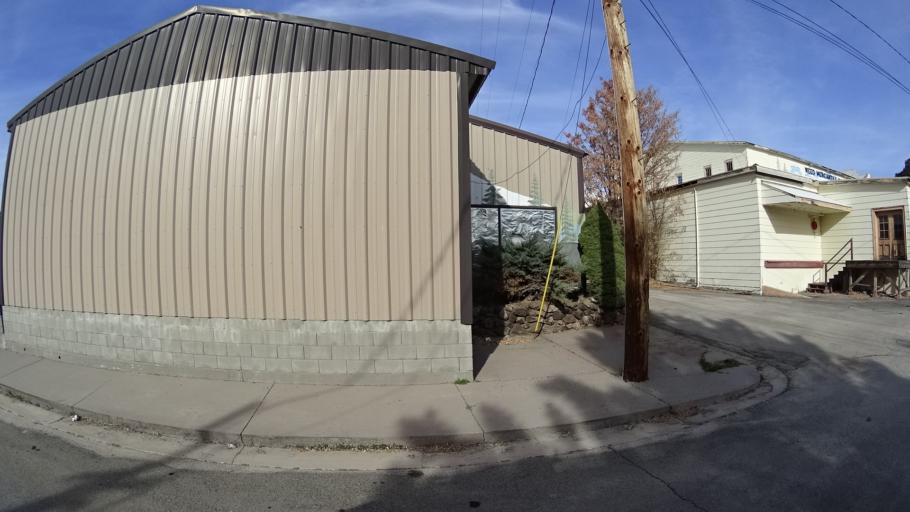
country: US
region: California
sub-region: Siskiyou County
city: Weed
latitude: 41.4280
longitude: -122.3849
